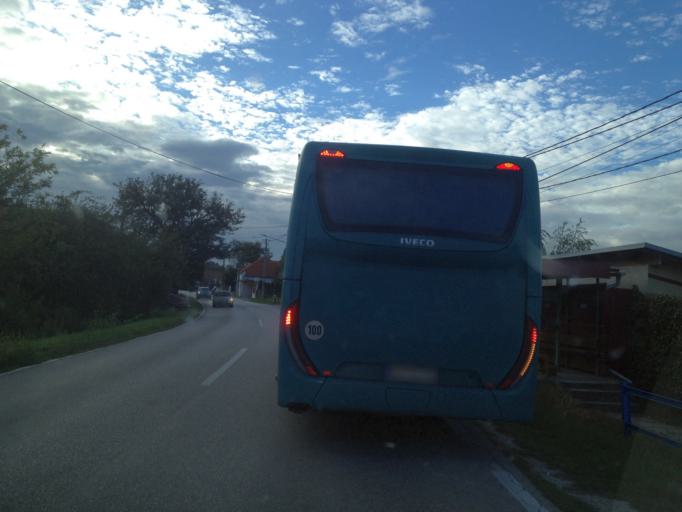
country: HU
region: Komarom-Esztergom
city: Almasfuzito
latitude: 47.7487
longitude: 18.2319
